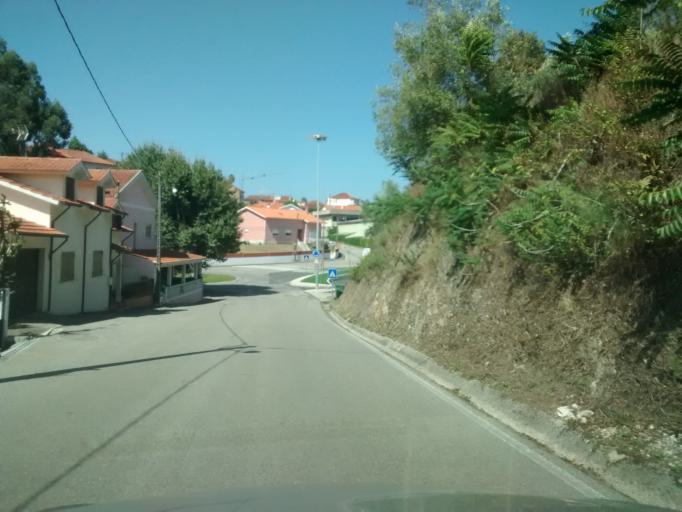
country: PT
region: Aveiro
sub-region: Mealhada
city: Pampilhosa do Botao
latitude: 40.3849
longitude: -8.3827
